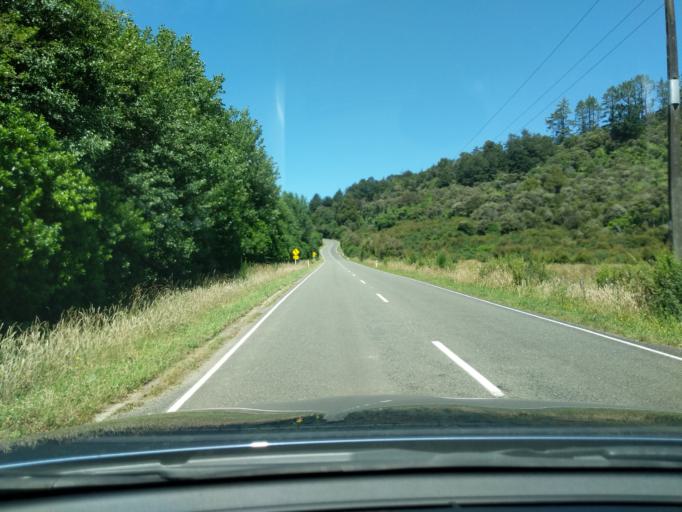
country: NZ
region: Tasman
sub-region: Tasman District
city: Takaka
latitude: -40.7234
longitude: 172.6019
